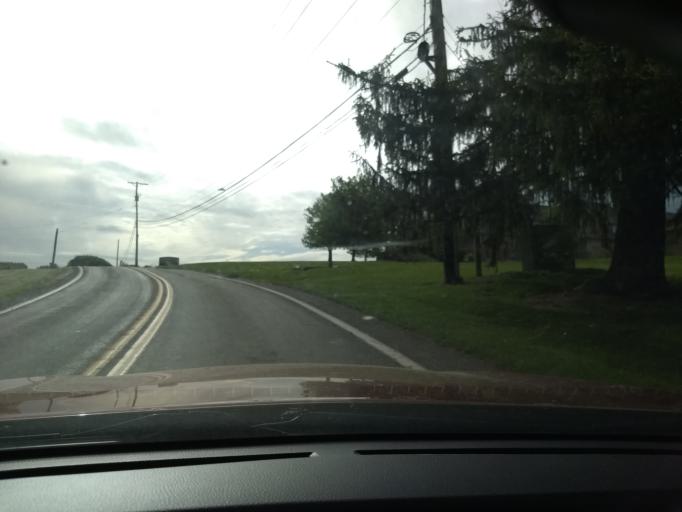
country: US
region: Pennsylvania
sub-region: Allegheny County
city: Russellton
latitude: 40.6016
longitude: -79.8973
